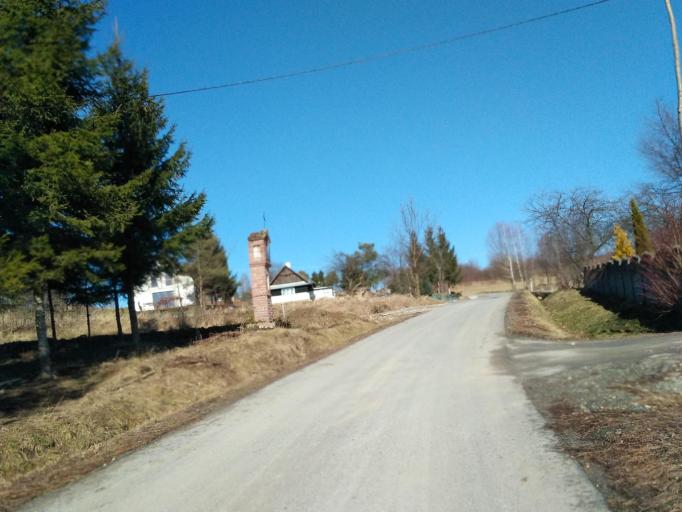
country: PL
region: Subcarpathian Voivodeship
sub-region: Powiat rzeszowski
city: Lubenia
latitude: 49.9319
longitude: 21.9460
